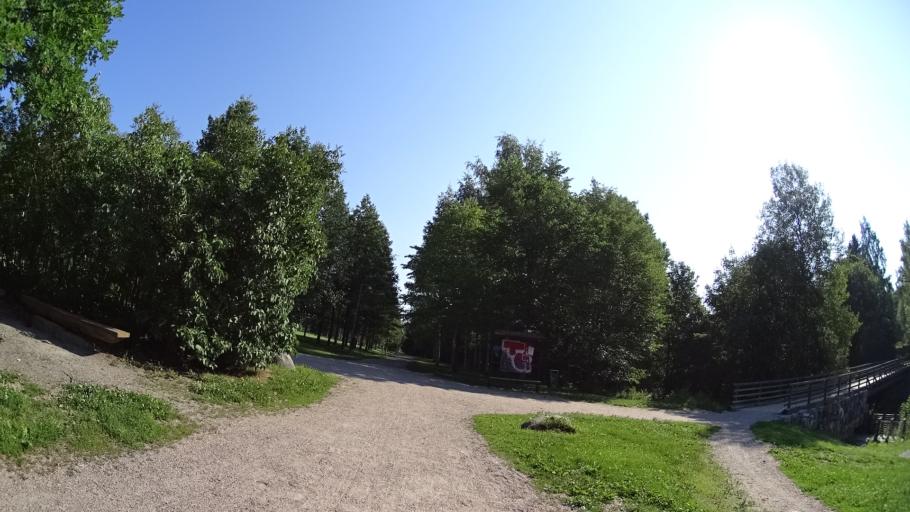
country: FI
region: Uusimaa
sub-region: Helsinki
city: Vantaa
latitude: 60.3195
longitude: 25.0831
